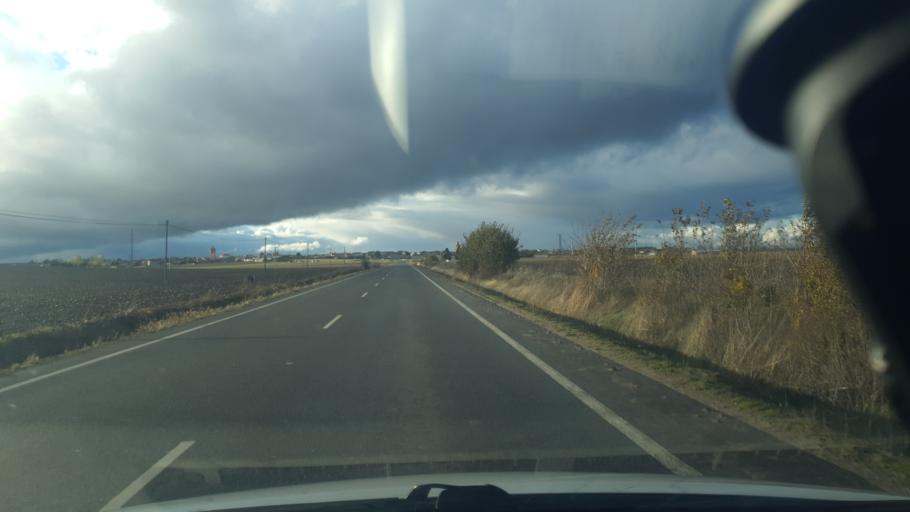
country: ES
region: Castille and Leon
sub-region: Provincia de Segovia
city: Santiuste de San Juan Bautista
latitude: 41.1527
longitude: -4.5578
